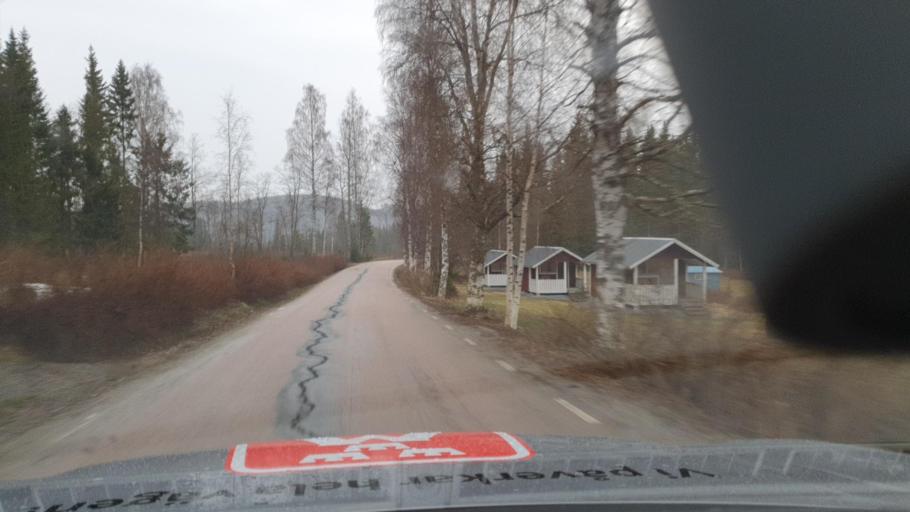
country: SE
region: Vaesternorrland
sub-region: OErnskoeldsviks Kommun
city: Bjasta
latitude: 63.2036
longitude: 18.4173
